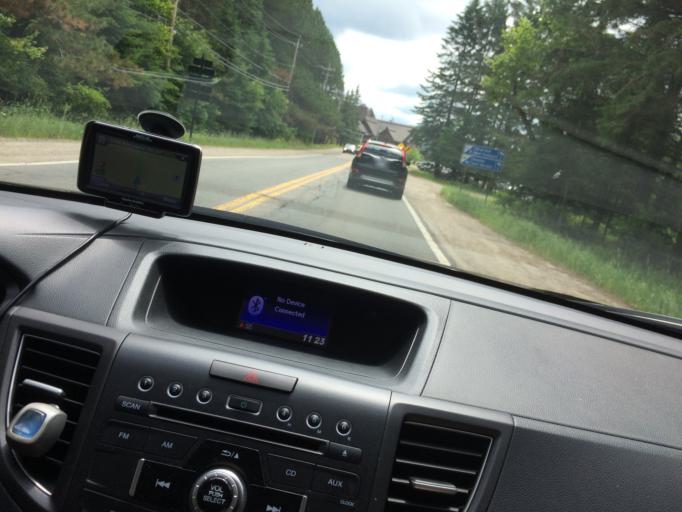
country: CA
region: Quebec
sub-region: Laurentides
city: Mont-Tremblant
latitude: 46.1738
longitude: -74.6006
